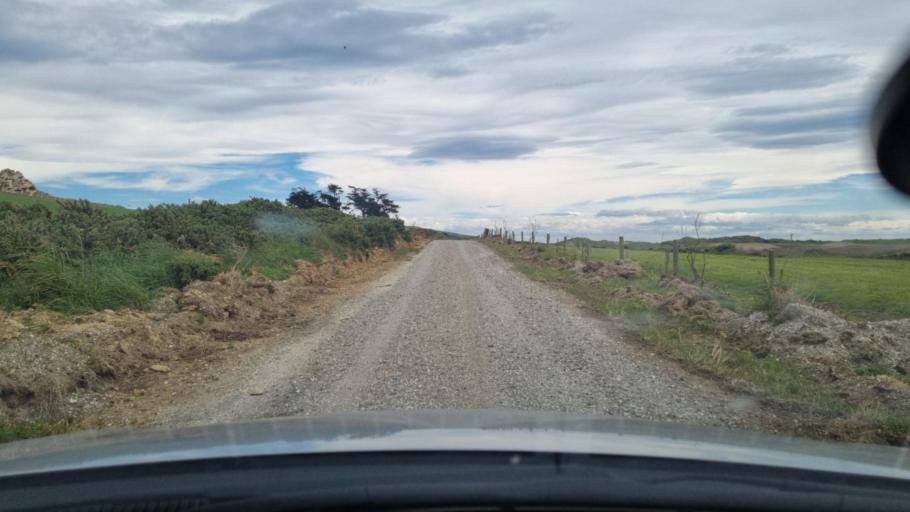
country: NZ
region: Southland
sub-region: Invercargill City
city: Bluff
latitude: -46.5201
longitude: 168.2960
